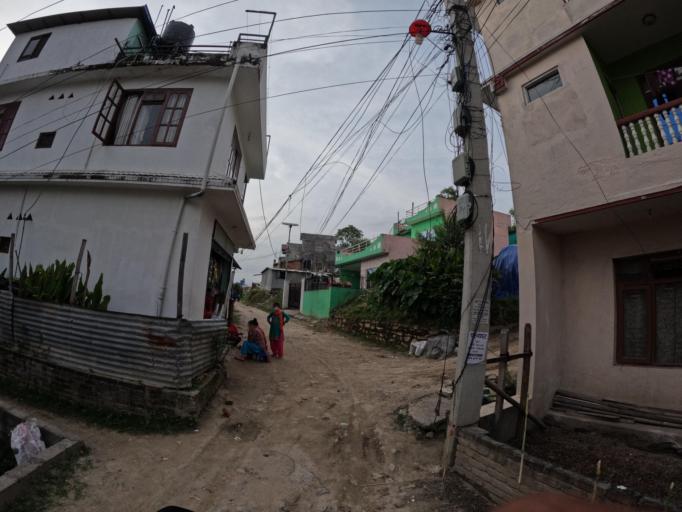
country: NP
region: Central Region
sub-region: Bagmati Zone
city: Bhaktapur
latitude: 27.6840
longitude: 85.3936
